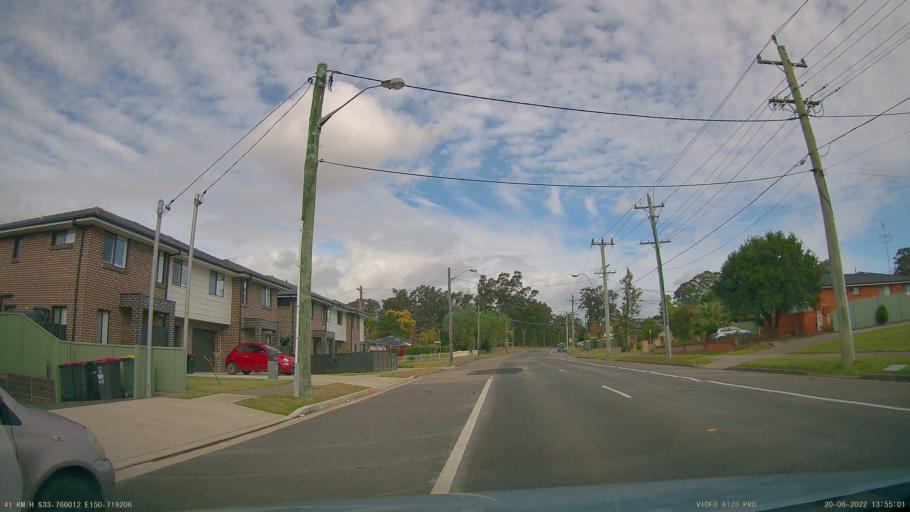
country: AU
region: New South Wales
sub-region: Penrith Municipality
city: Kingswood Park
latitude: -33.7661
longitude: 150.7192
